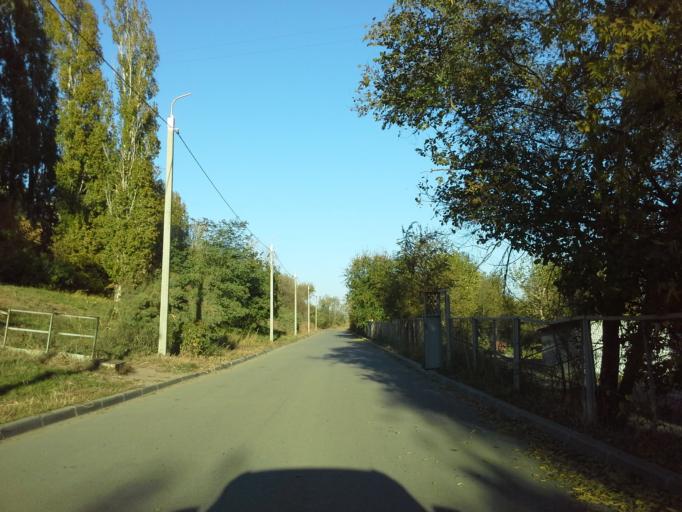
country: RU
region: Volgograd
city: Vodstroy
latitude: 48.8200
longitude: 44.6407
